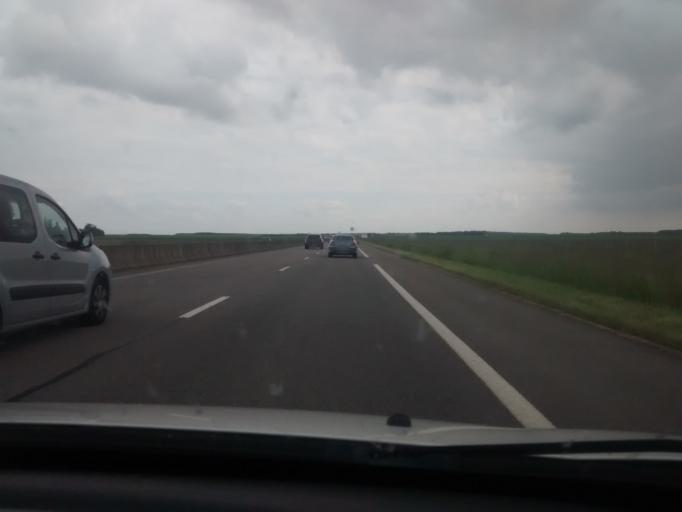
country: FR
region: Ile-de-France
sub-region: Departement des Yvelines
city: Sonchamp
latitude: 48.5888
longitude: 1.8320
